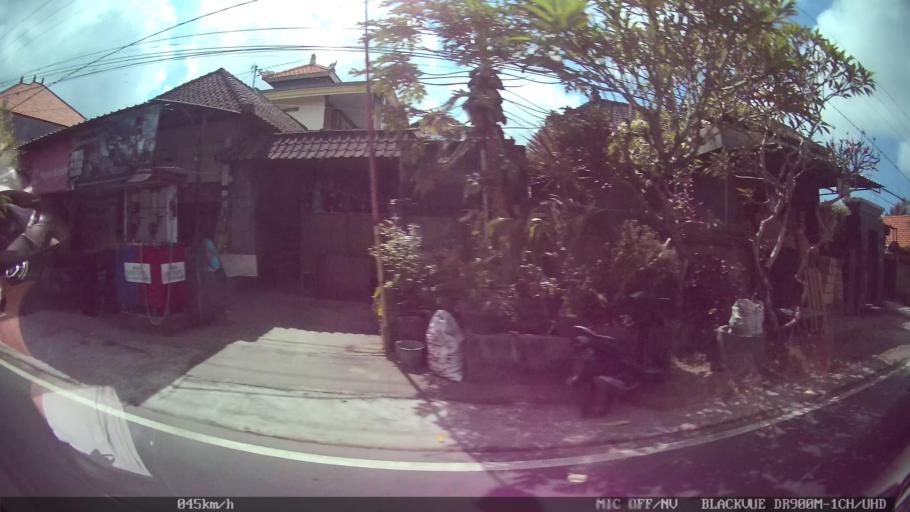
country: ID
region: Bali
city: Banjar Pasekan
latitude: -8.5888
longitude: 115.2966
